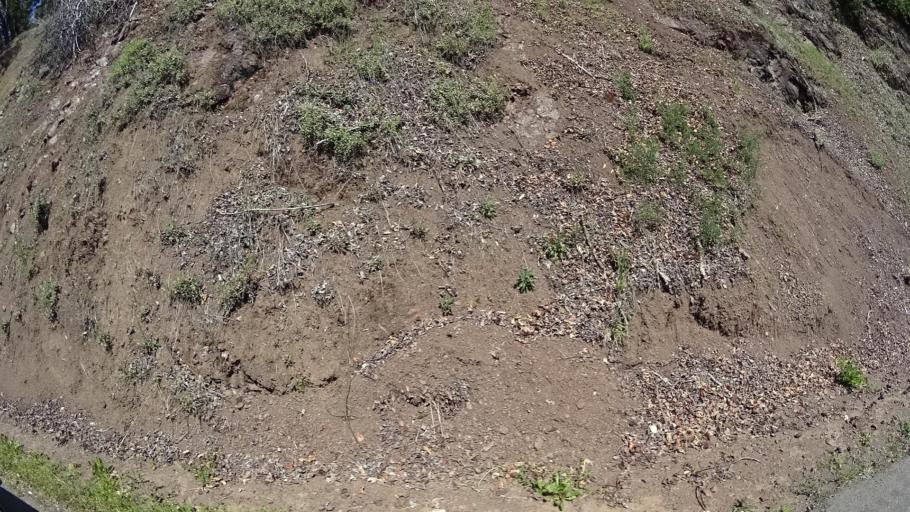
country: US
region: California
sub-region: Humboldt County
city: Redway
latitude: 40.2634
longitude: -123.6269
